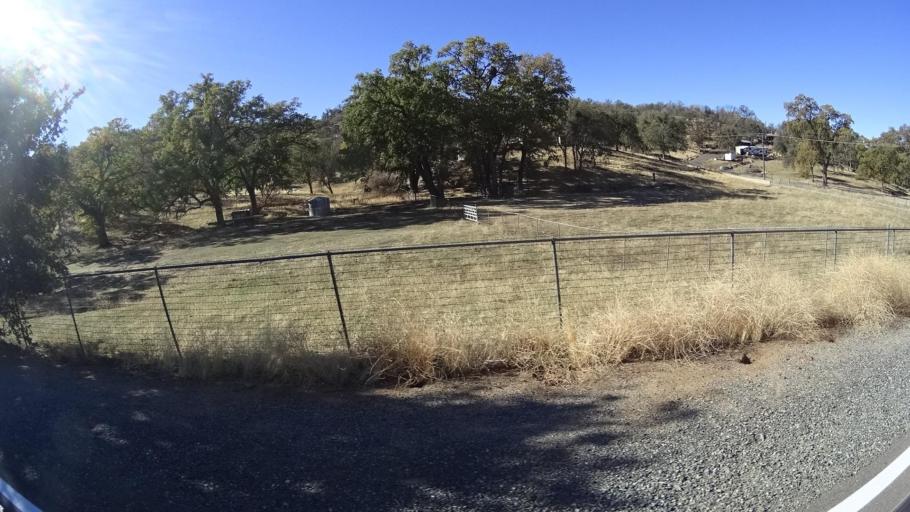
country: US
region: California
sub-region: Kern County
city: Alta Sierra
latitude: 35.7241
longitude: -118.6974
